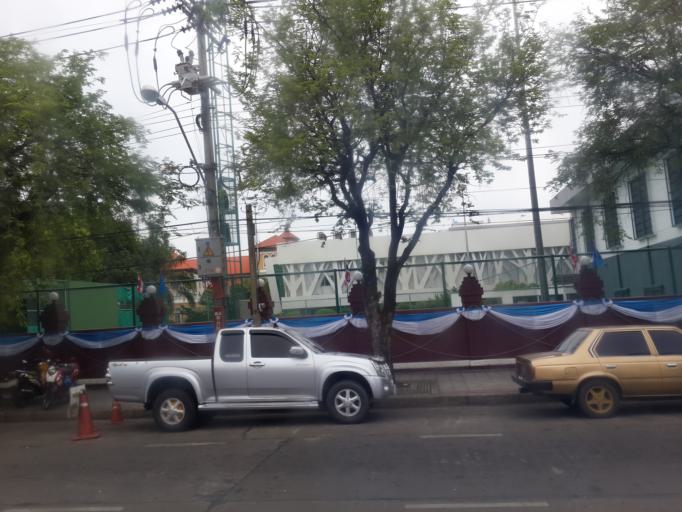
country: TH
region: Bangkok
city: Phra Nakhon
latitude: 13.7688
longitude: 100.5069
